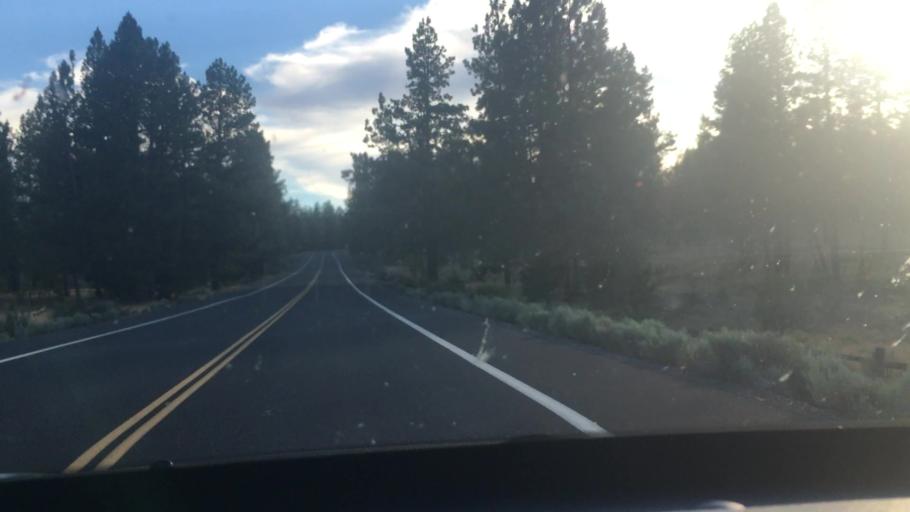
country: US
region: Oregon
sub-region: Deschutes County
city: Deschutes River Woods
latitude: 44.0510
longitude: -121.3804
